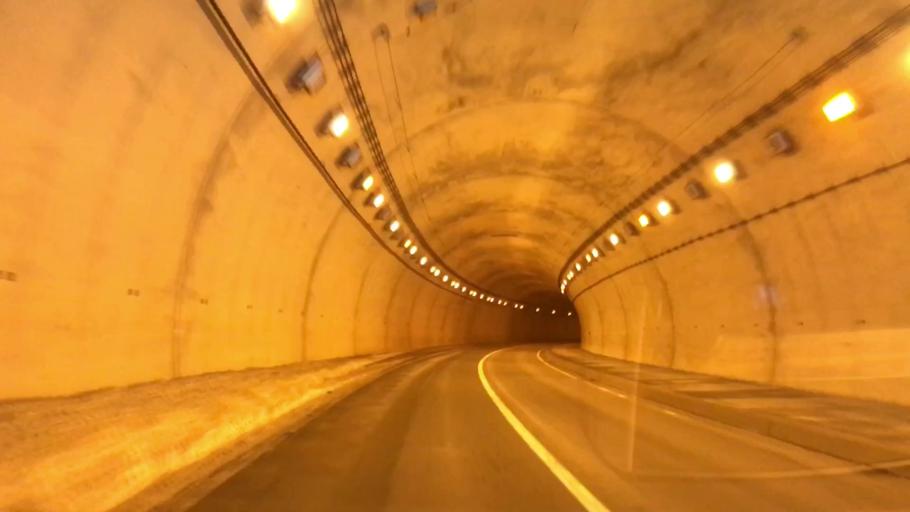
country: JP
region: Hokkaido
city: Yoichi
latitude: 43.2944
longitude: 140.6263
